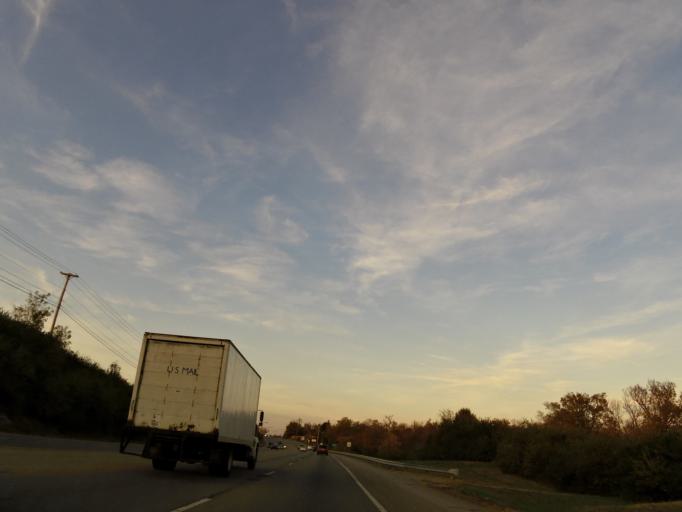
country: US
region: Kentucky
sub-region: Fayette County
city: Monticello
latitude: 37.9616
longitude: -84.5365
